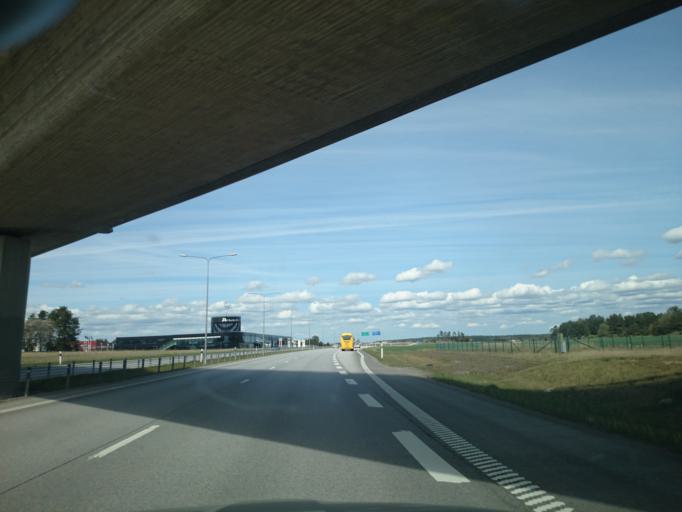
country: SE
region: Uppsala
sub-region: Uppsala Kommun
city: Saevja
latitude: 59.8368
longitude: 17.7325
